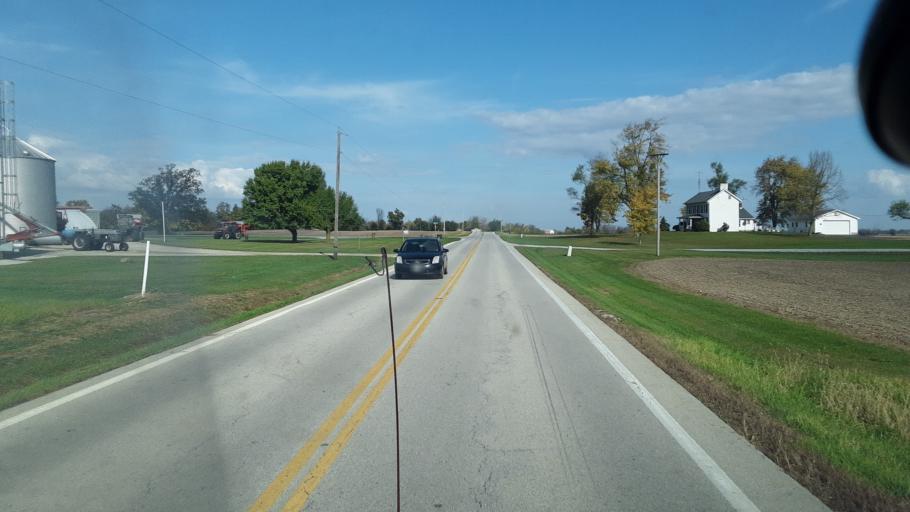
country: US
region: Ohio
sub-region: Clinton County
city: Sabina
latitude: 39.5058
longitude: -83.6869
